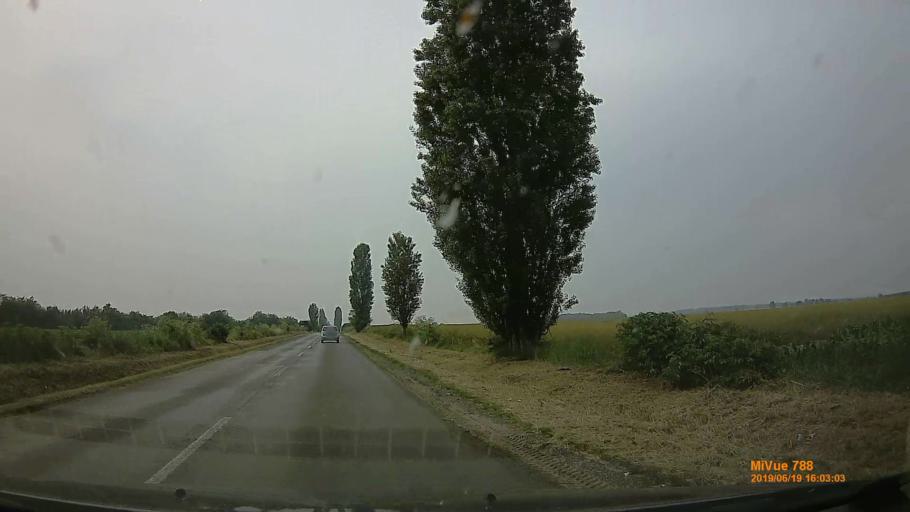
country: HU
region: Baranya
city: Szigetvar
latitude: 46.0645
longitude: 17.7720
